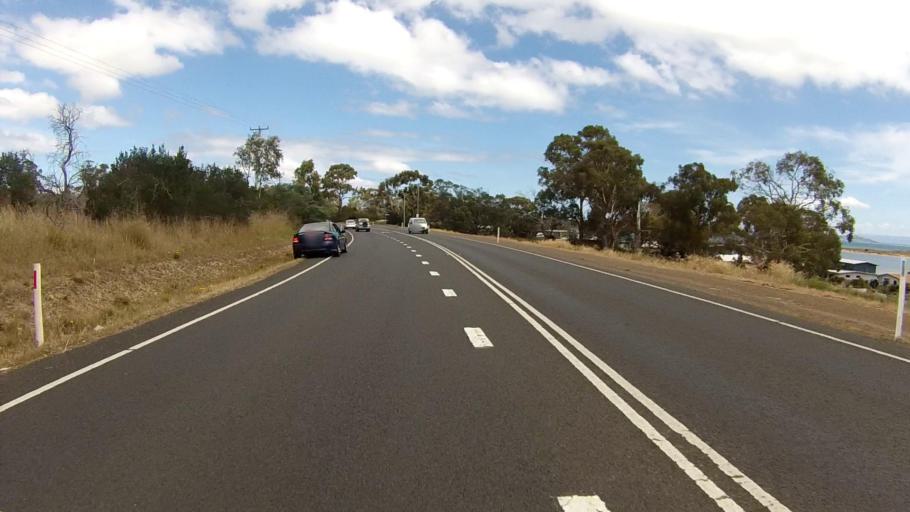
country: AU
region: Tasmania
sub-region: Sorell
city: Sorell
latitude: -42.8394
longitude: 147.6226
